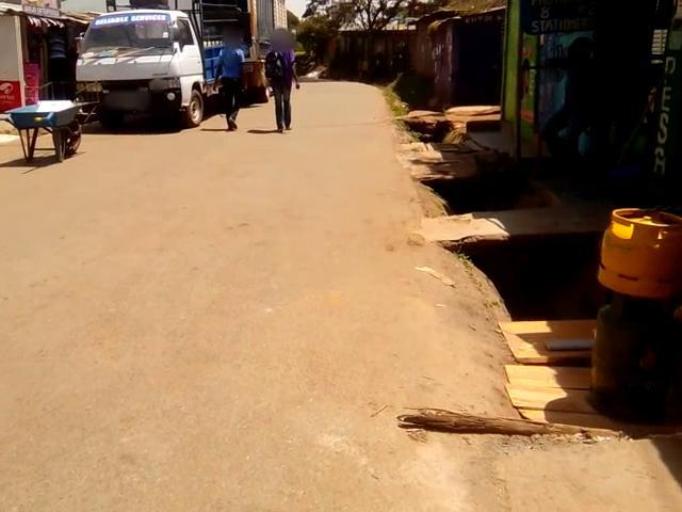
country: KE
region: Nairobi Area
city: Nairobi
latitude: -1.3166
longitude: 36.7750
